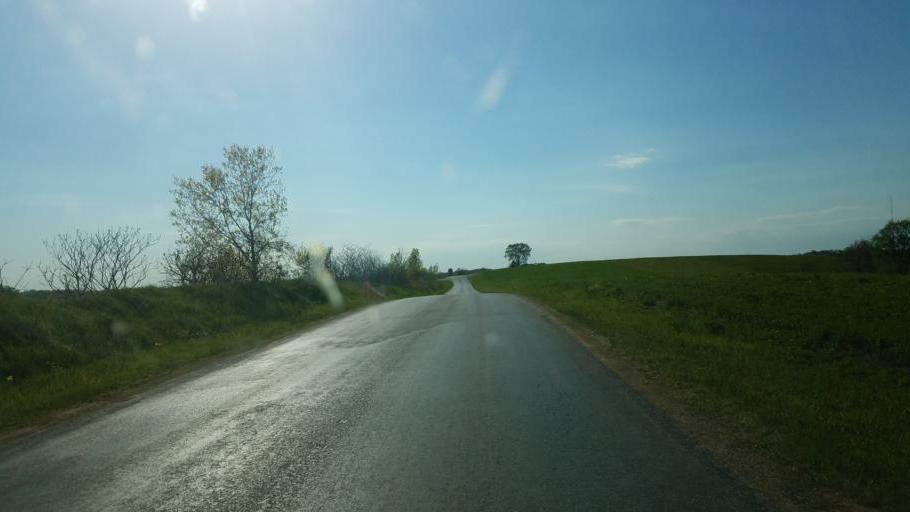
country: US
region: Wisconsin
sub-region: Vernon County
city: Hillsboro
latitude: 43.6841
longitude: -90.3779
